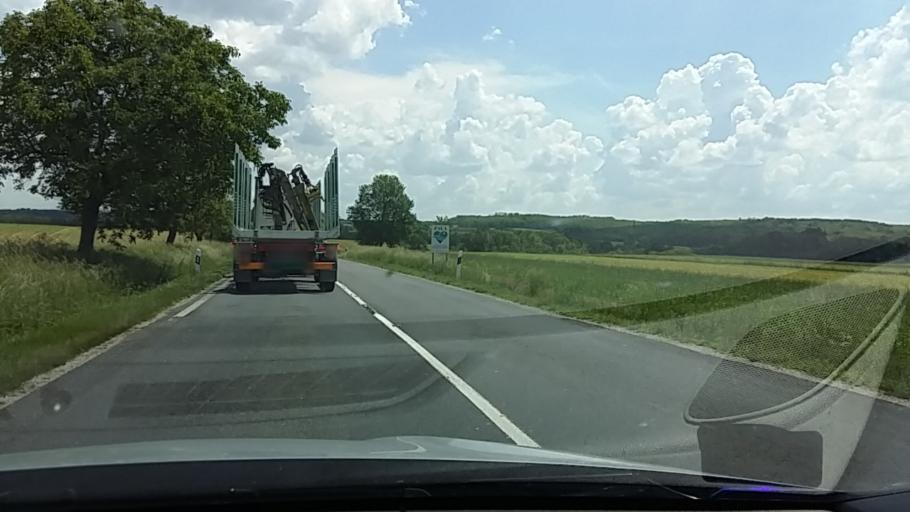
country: HU
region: Vas
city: Kormend
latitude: 46.9330
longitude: 16.6738
